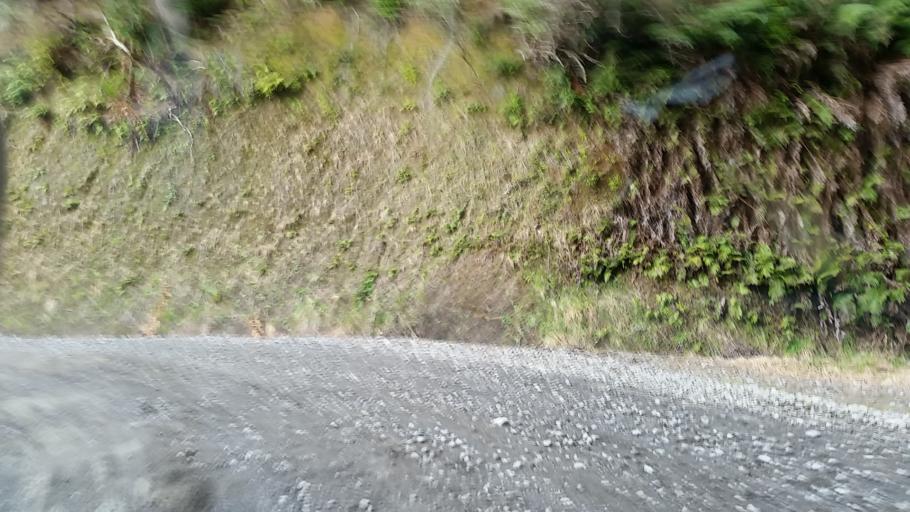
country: NZ
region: Taranaki
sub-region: New Plymouth District
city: Waitara
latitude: -39.1589
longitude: 174.5562
